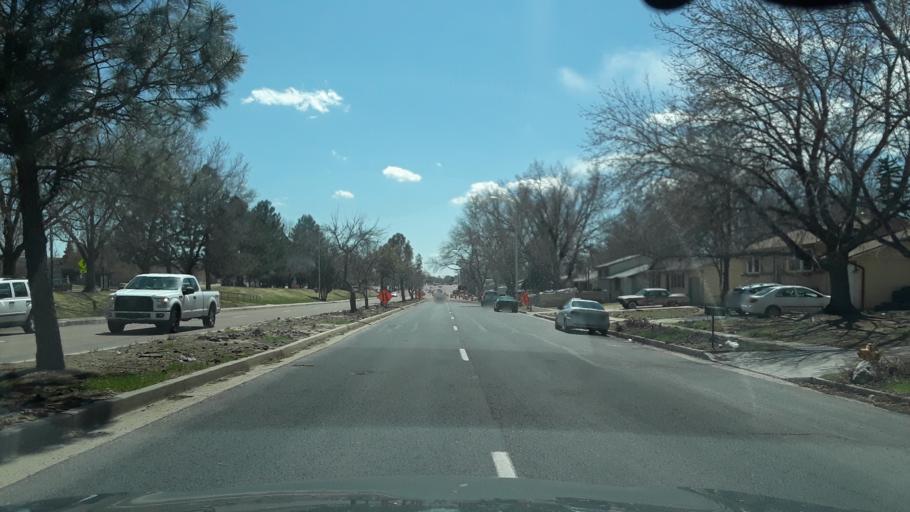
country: US
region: Colorado
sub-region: El Paso County
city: Colorado Springs
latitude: 38.8446
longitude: -104.7666
